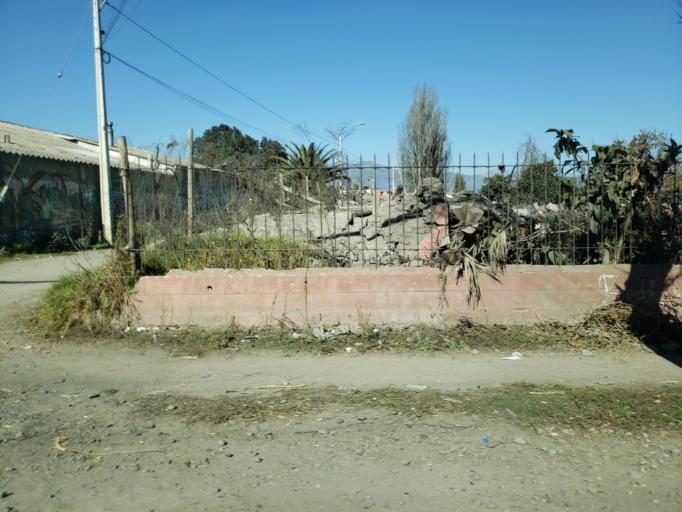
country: CL
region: Santiago Metropolitan
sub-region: Provincia de Talagante
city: El Monte
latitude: -33.6853
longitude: -71.0140
